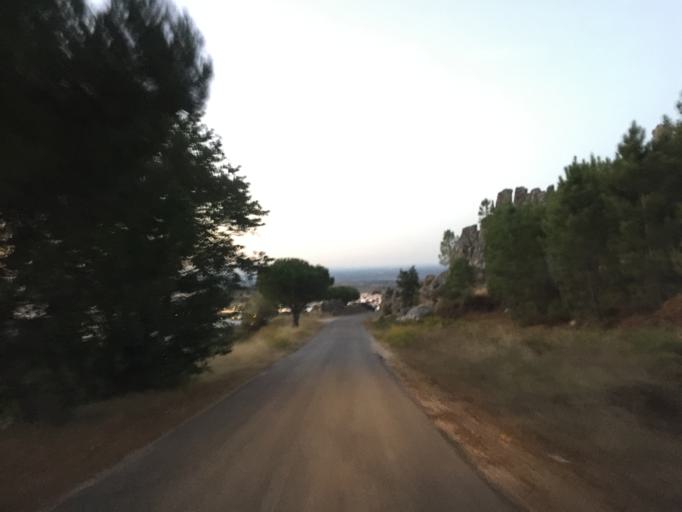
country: PT
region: Portalegre
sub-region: Castelo de Vide
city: Castelo de Vide
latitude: 39.4019
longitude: -7.4495
